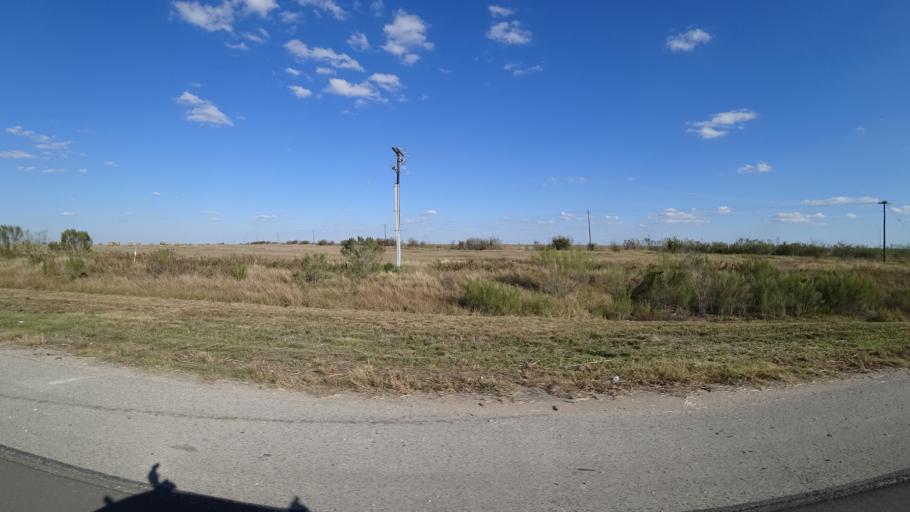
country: US
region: Texas
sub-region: Travis County
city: Onion Creek
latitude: 30.0902
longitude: -97.6936
